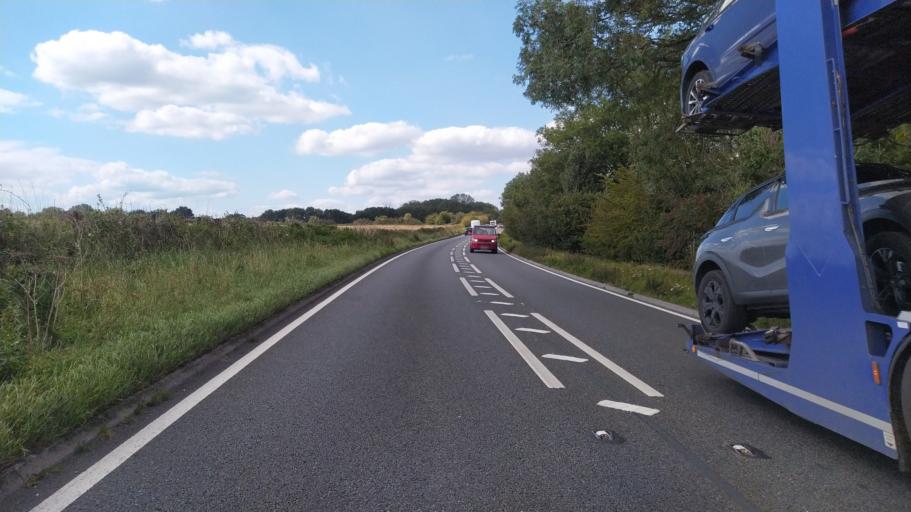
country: GB
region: England
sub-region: Wiltshire
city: Stockton
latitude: 51.1204
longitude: -2.0283
